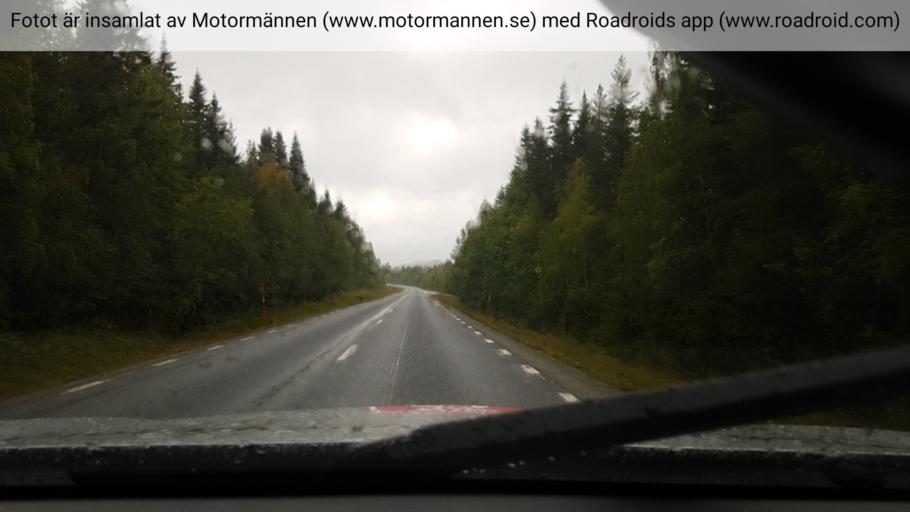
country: SE
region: Vaesterbotten
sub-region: Lycksele Kommun
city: Lycksele
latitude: 64.0505
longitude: 18.5610
